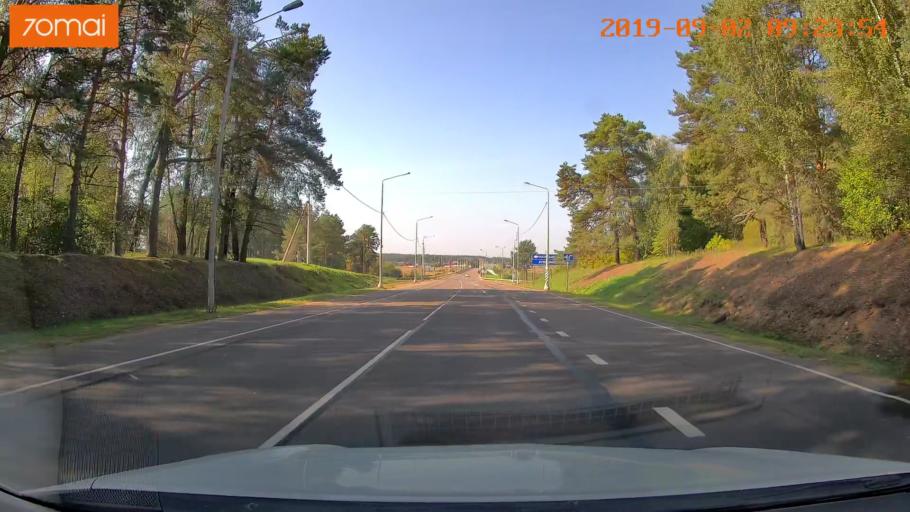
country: RU
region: Kaluga
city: Yukhnov
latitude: 54.7714
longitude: 35.3052
